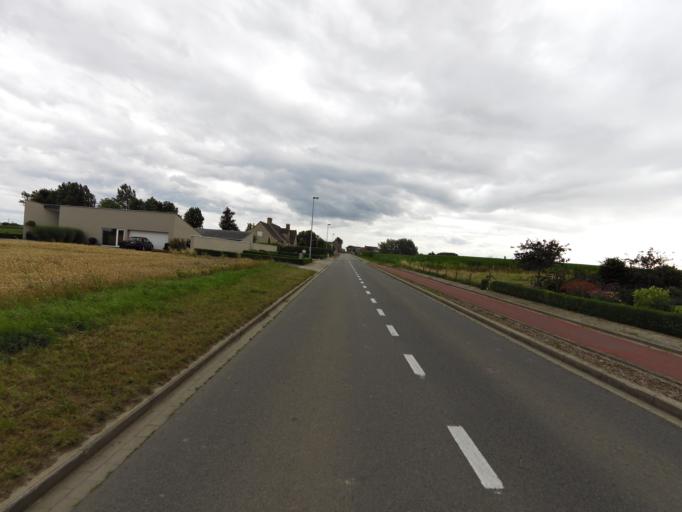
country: BE
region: Flanders
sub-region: Provincie West-Vlaanderen
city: Staden
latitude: 50.9929
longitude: 3.0341
